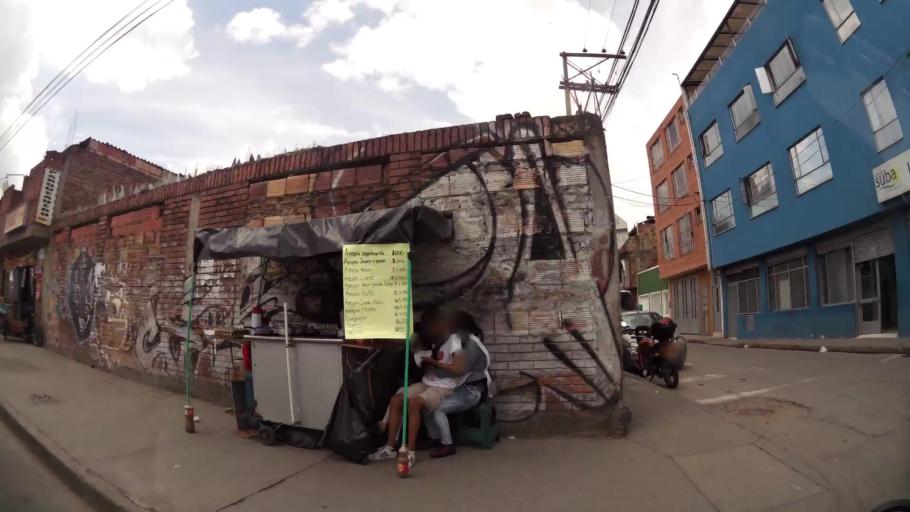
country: CO
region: Cundinamarca
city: Cota
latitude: 4.7262
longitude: -74.0934
